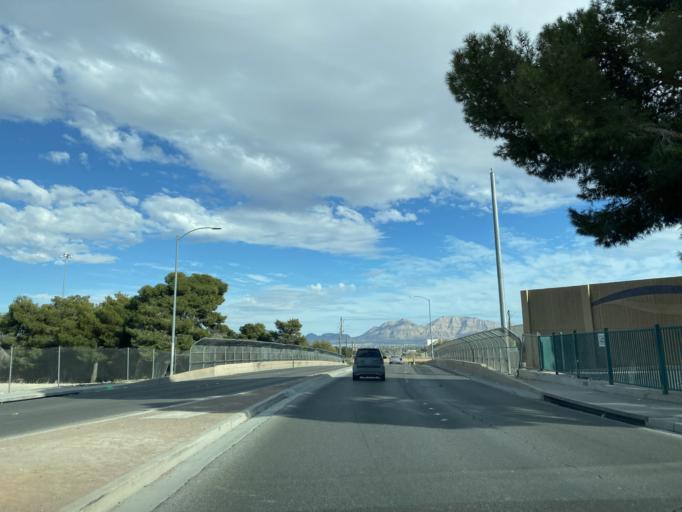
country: US
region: Nevada
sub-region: Clark County
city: Las Vegas
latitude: 36.1883
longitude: -115.1441
